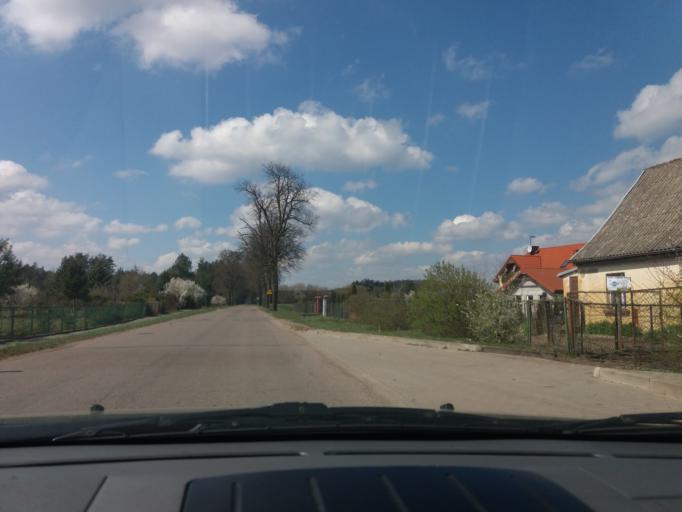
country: PL
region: Warmian-Masurian Voivodeship
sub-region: Powiat szczycienski
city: Jedwabno
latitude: 53.3635
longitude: 20.6347
